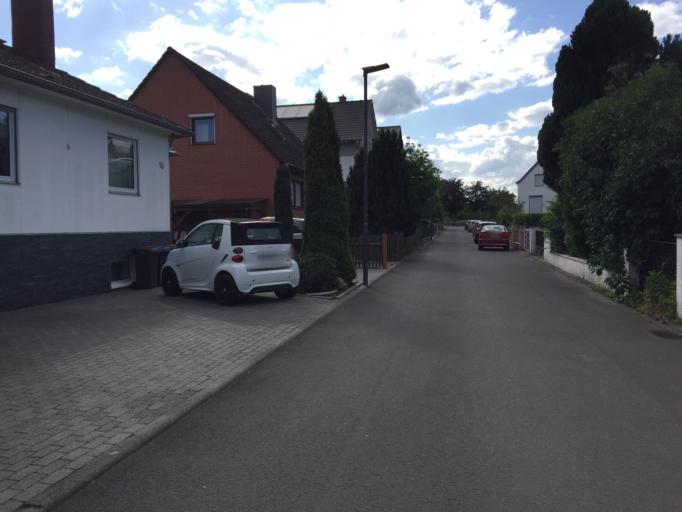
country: DE
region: Hesse
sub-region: Regierungsbezirk Darmstadt
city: Karben
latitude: 50.2453
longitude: 8.7538
